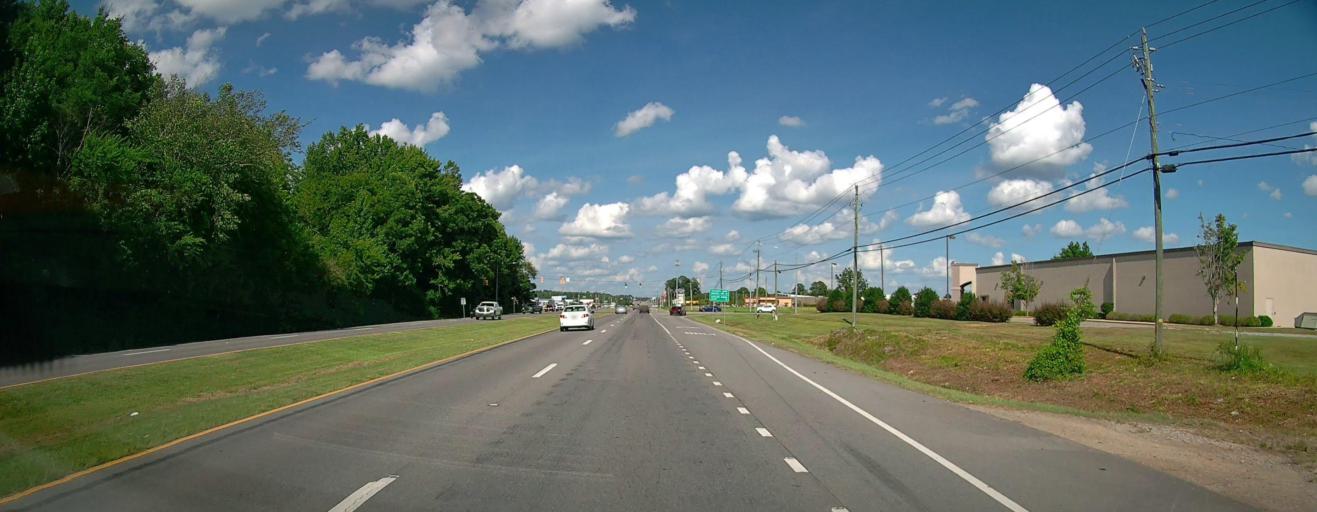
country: US
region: Alabama
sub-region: Tuscaloosa County
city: Northport
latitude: 33.2334
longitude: -87.6202
